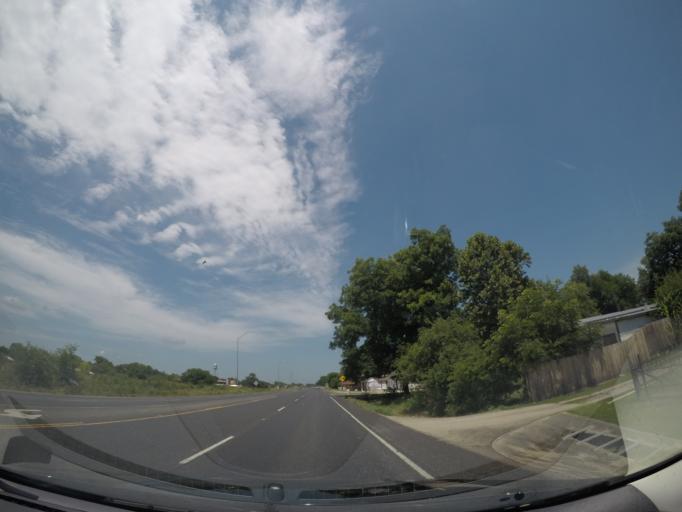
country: US
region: Texas
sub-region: Medina County
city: Hondo
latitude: 29.3293
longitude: -99.2835
